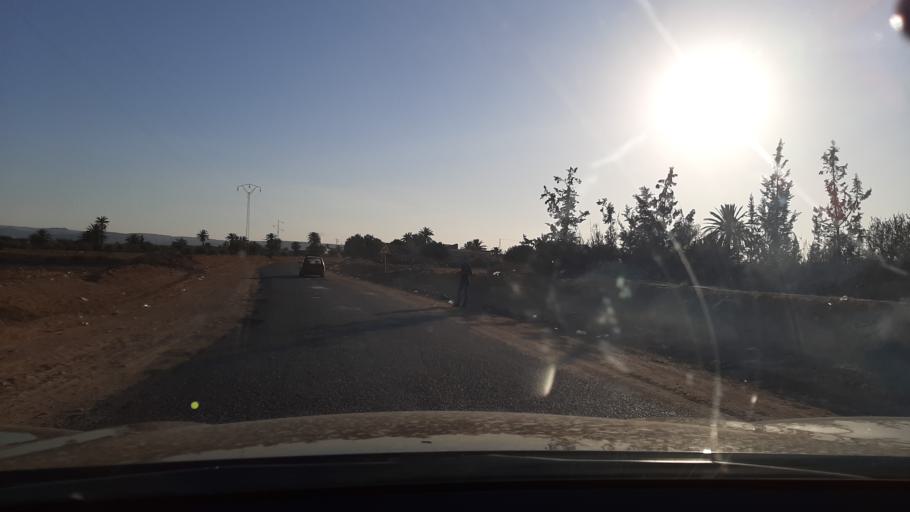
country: TN
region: Qabis
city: Matmata
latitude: 33.6192
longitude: 10.2693
